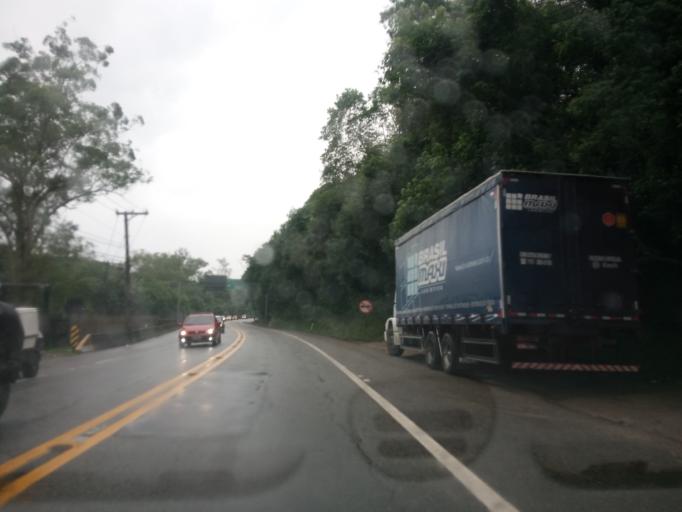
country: BR
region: Sao Paulo
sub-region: Sao Bernardo Do Campo
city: Sao Bernardo do Campo
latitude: -23.7824
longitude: -46.5069
